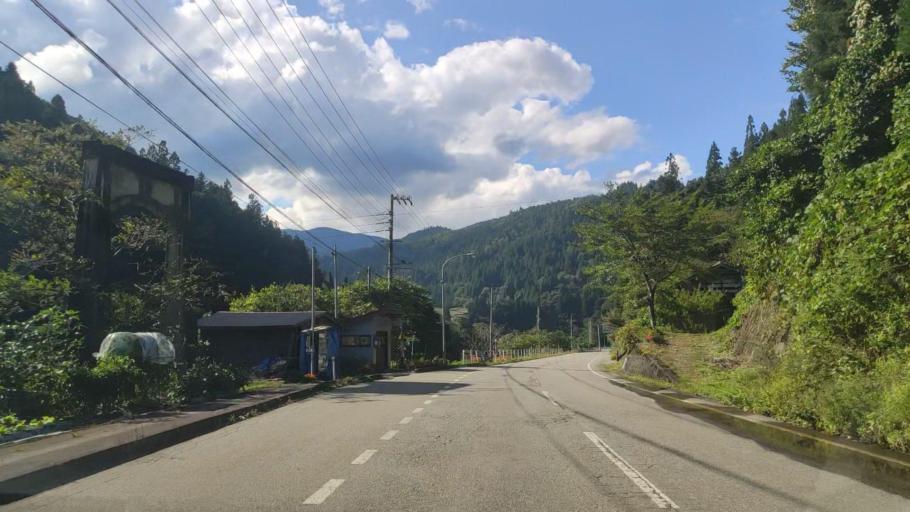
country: JP
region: Gifu
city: Takayama
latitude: 36.3031
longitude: 137.1129
